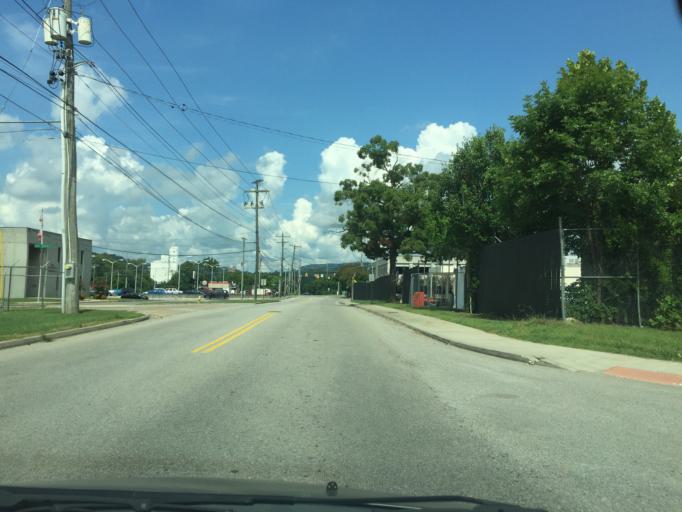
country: US
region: Tennessee
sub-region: Hamilton County
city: East Chattanooga
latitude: 35.0805
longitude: -85.2620
